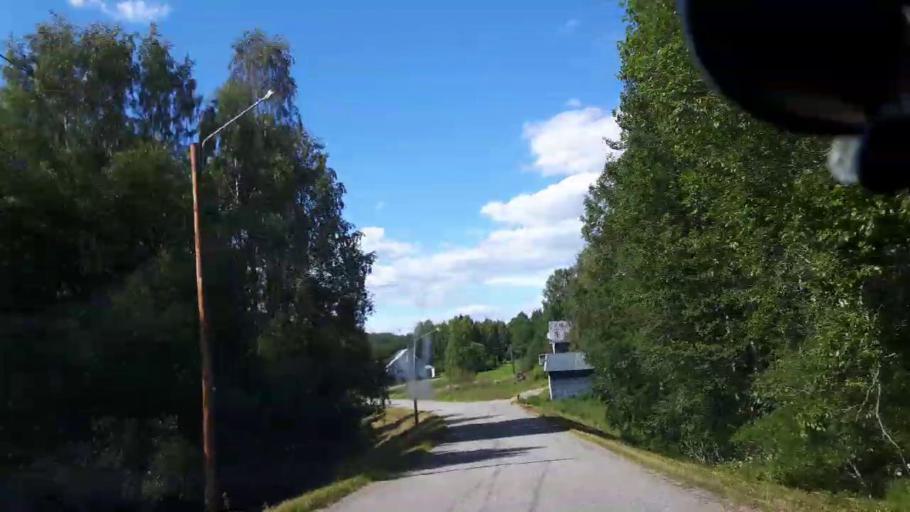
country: SE
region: Vaesternorrland
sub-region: Ange Kommun
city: Fransta
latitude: 62.7804
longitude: 16.0044
